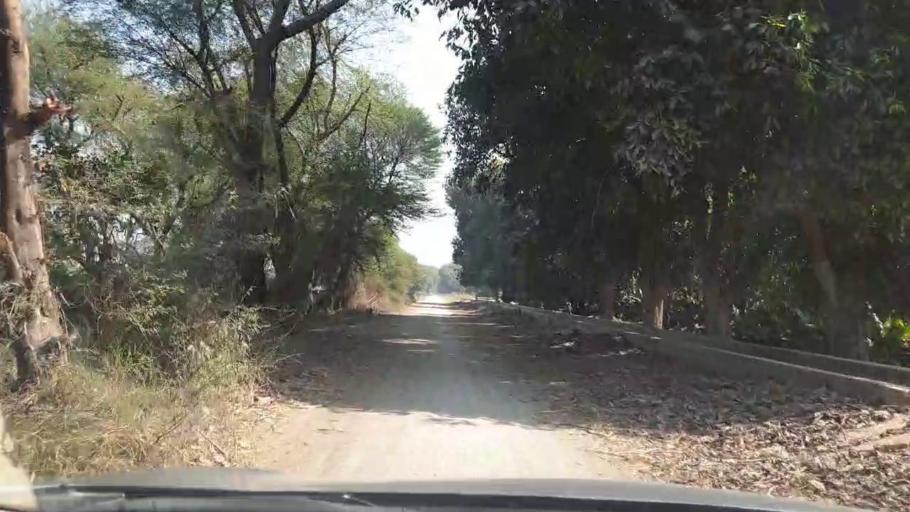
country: PK
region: Sindh
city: Tando Allahyar
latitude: 25.4903
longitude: 68.7710
